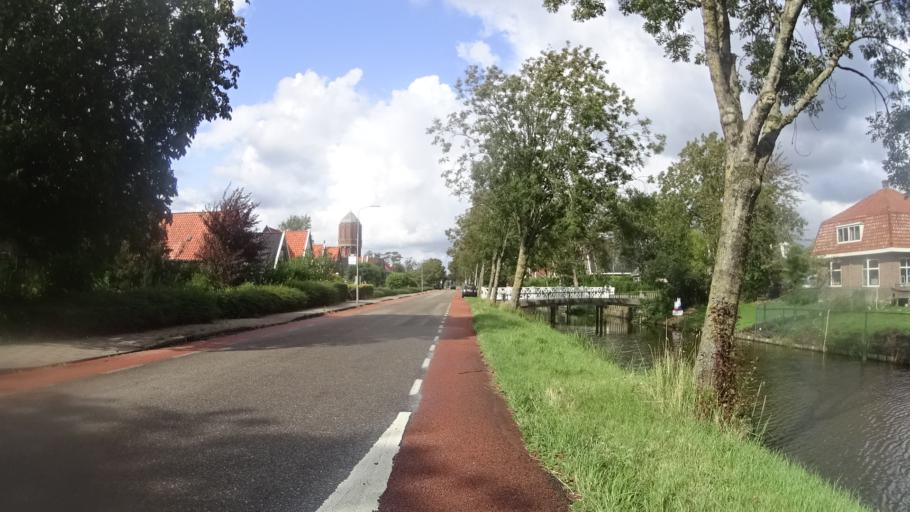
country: NL
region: North Holland
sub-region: Gemeente Schagen
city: Schagen
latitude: 52.8374
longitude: 4.8606
